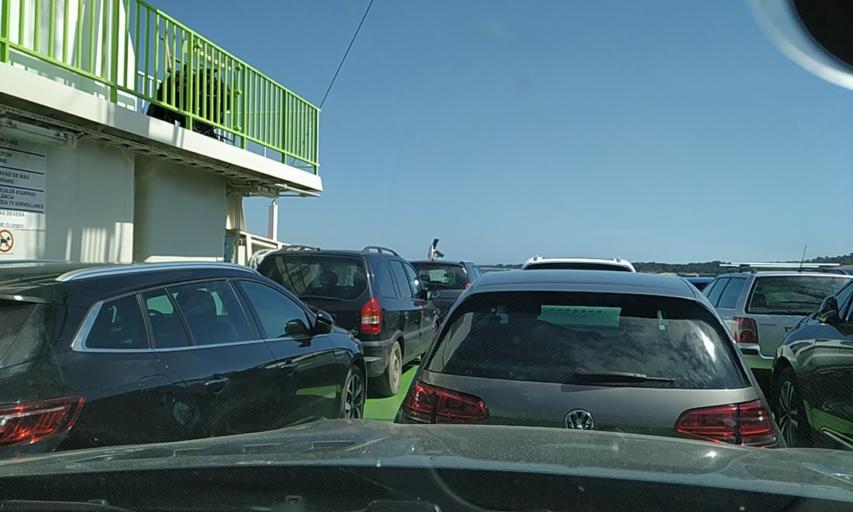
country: PT
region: Setubal
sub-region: Setubal
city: Setubal
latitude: 38.4794
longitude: -8.8717
